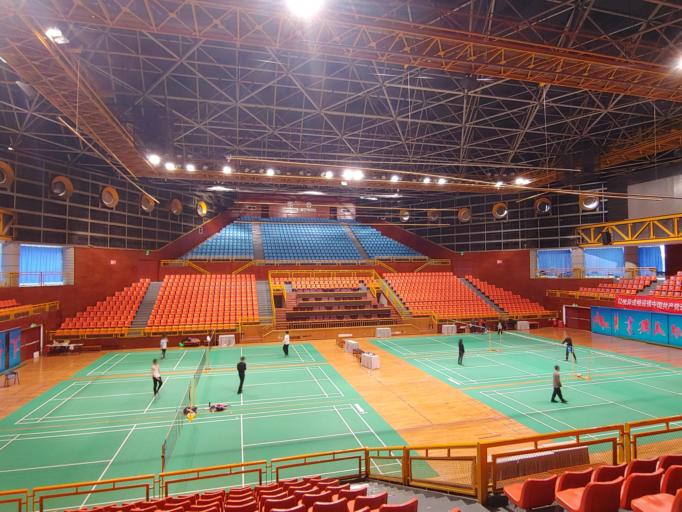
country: CN
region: Yunnan
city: Kunming
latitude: 25.0513
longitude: 102.6882
